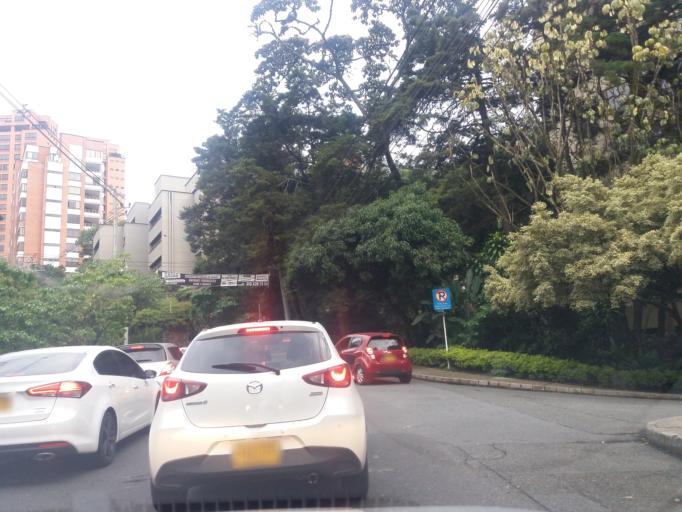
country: CO
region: Antioquia
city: Itagui
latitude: 6.2067
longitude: -75.5690
